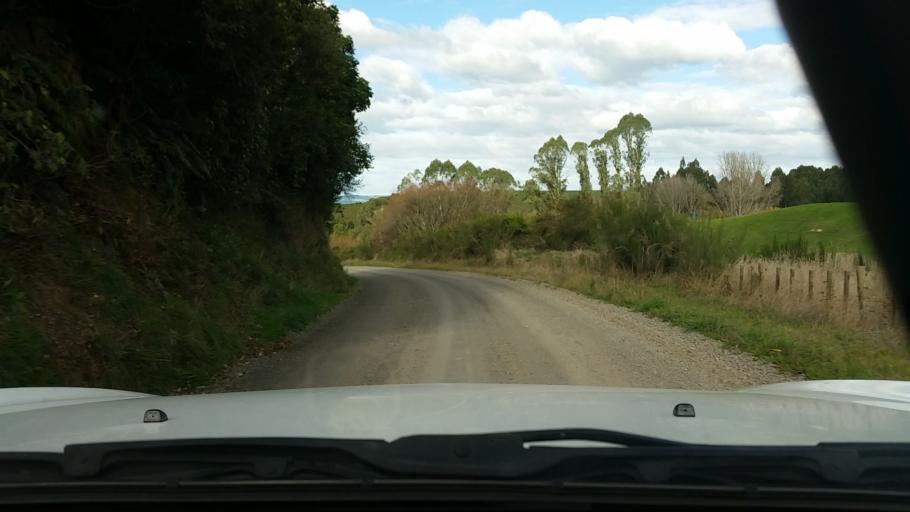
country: NZ
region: Waikato
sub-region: Taupo District
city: Taupo
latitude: -38.4897
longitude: 176.1898
